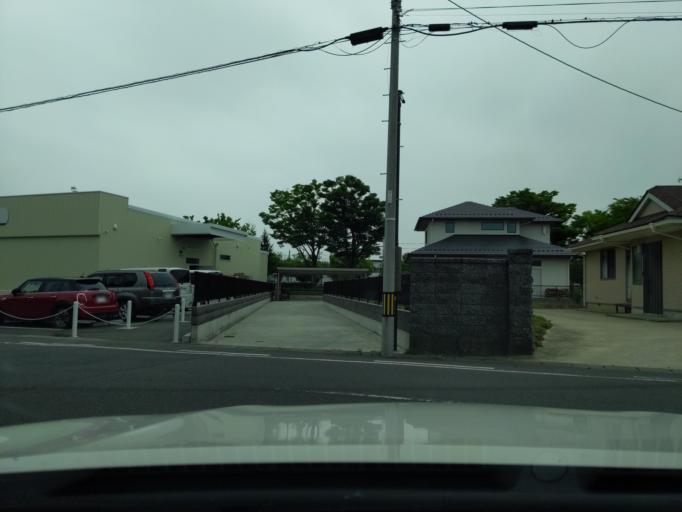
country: JP
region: Fukushima
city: Koriyama
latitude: 37.3551
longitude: 140.3629
